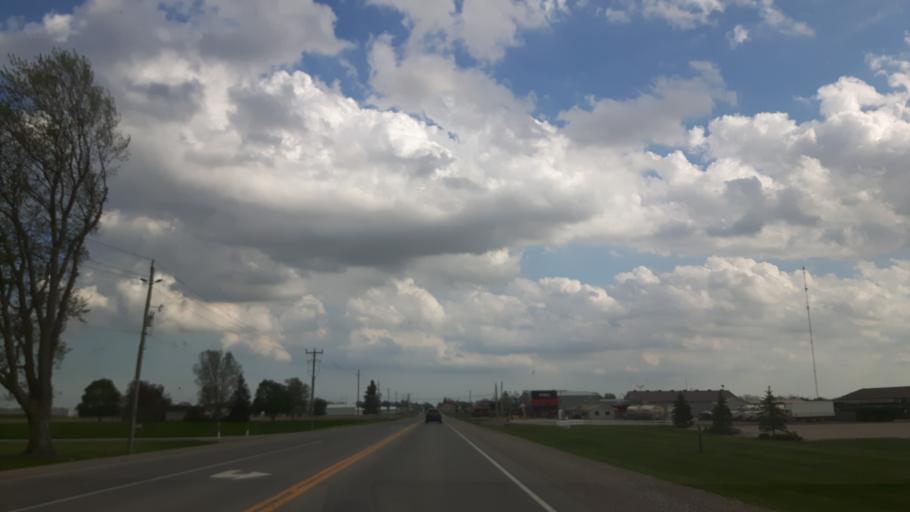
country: CA
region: Ontario
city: South Huron
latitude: 43.3684
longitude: -81.4850
